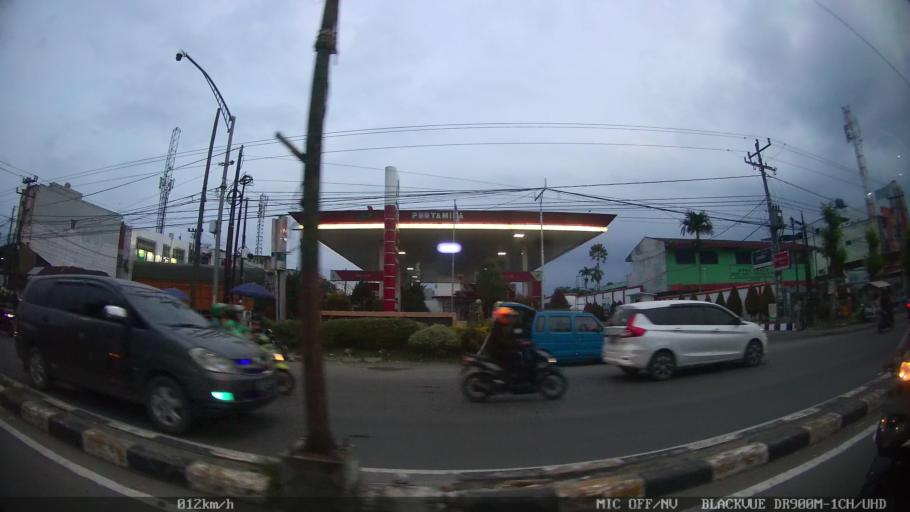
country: ID
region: North Sumatra
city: Sunggal
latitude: 3.5912
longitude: 98.6330
